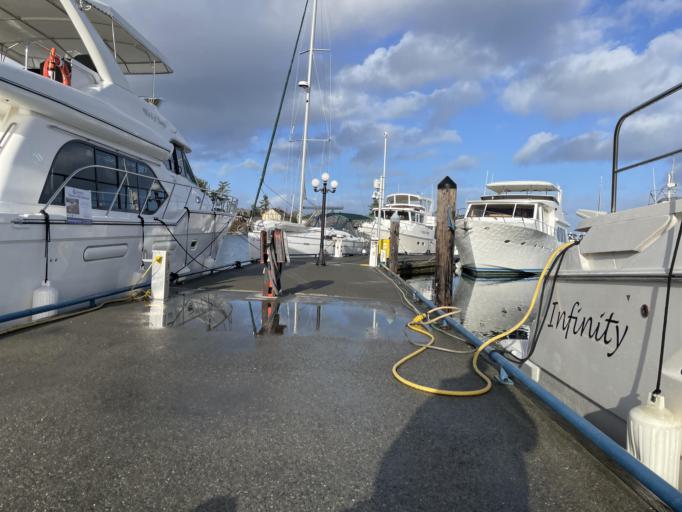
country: CA
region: British Columbia
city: North Saanich
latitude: 48.6522
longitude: -123.3954
